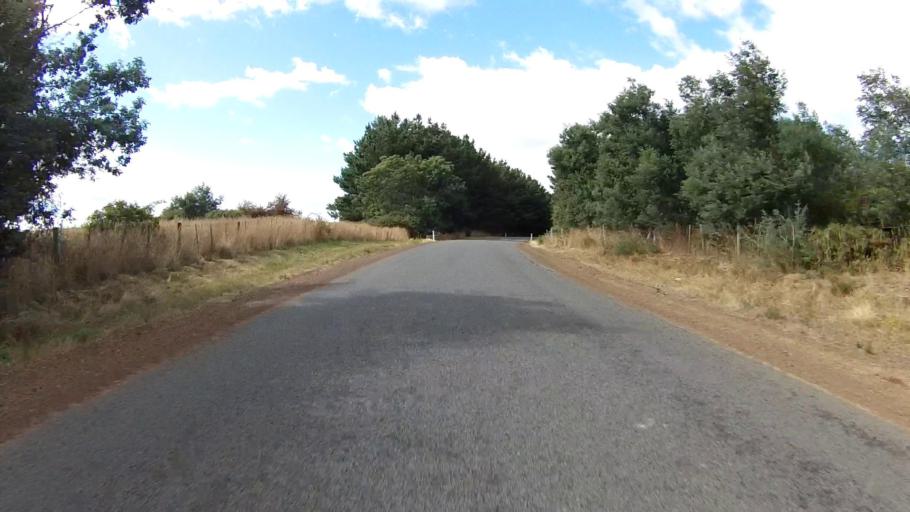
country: AU
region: Tasmania
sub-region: Northern Midlands
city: Evandale
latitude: -41.6931
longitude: 147.3657
